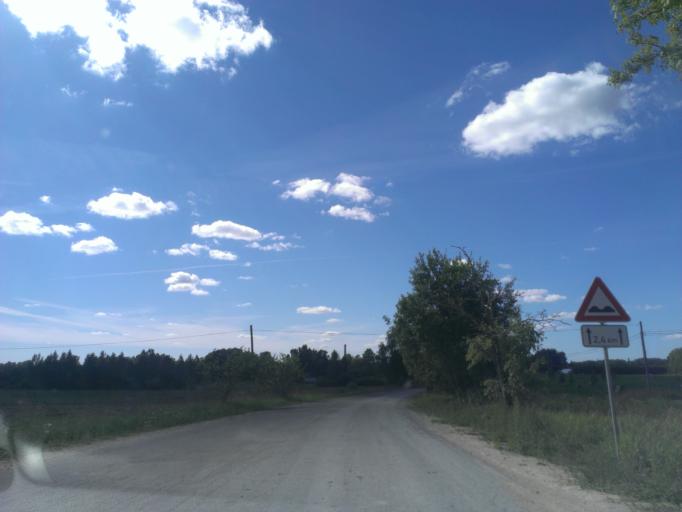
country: LV
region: Malpils
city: Malpils
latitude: 57.0136
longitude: 24.9804
